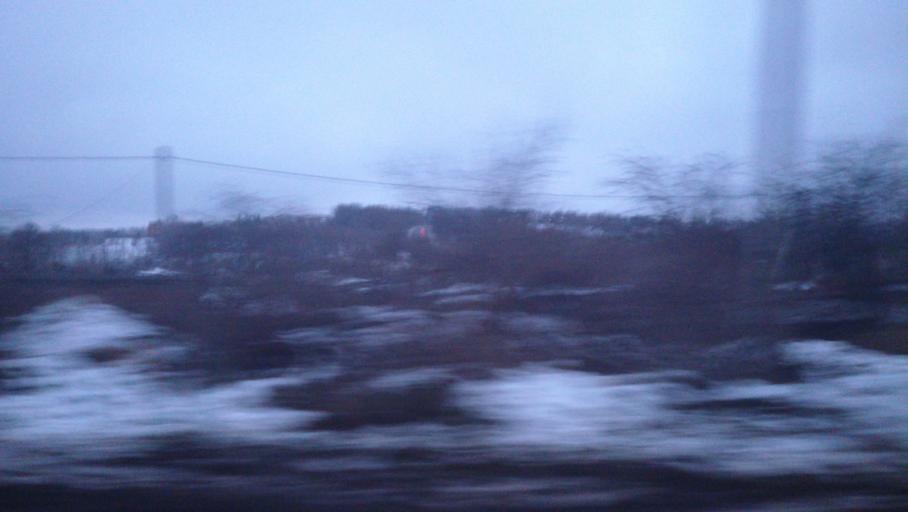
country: RU
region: Tula
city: Barsuki
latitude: 54.2044
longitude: 37.5351
